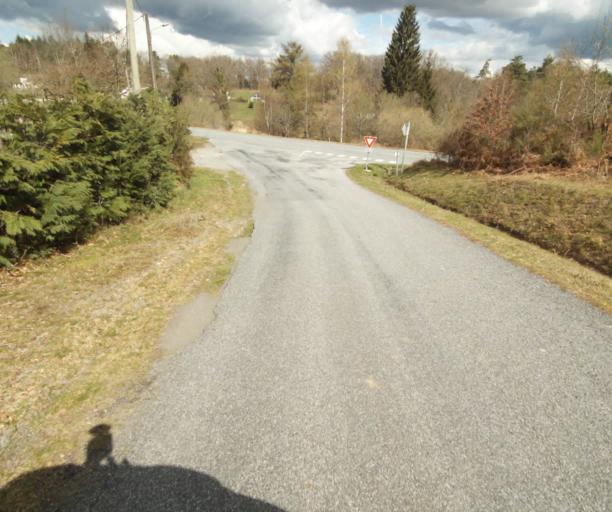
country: FR
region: Limousin
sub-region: Departement de la Correze
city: Correze
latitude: 45.2889
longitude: 1.8998
